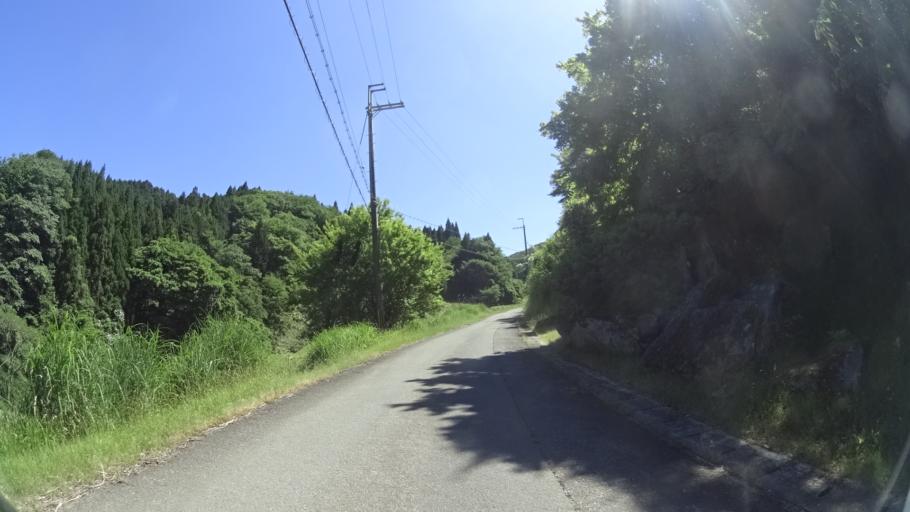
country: JP
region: Kyoto
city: Fukuchiyama
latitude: 35.3828
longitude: 135.0362
